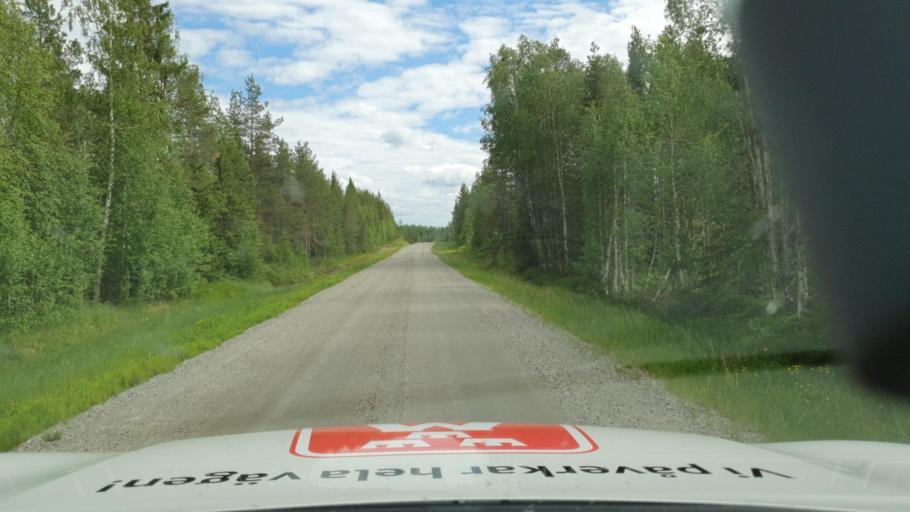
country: SE
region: Vaesterbotten
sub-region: Norsjo Kommun
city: Norsjoe
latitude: 64.8496
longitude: 19.5141
